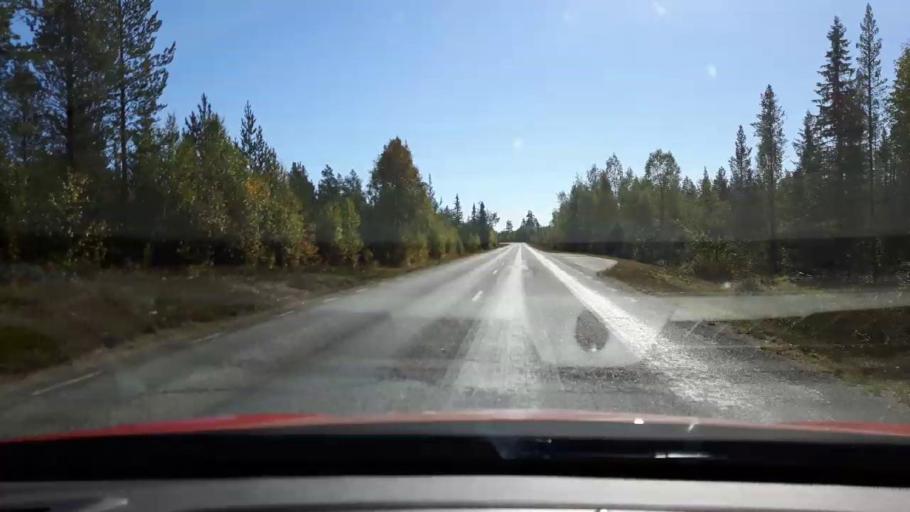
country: SE
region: Jaemtland
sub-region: Harjedalens Kommun
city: Sveg
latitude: 62.3674
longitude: 13.9901
